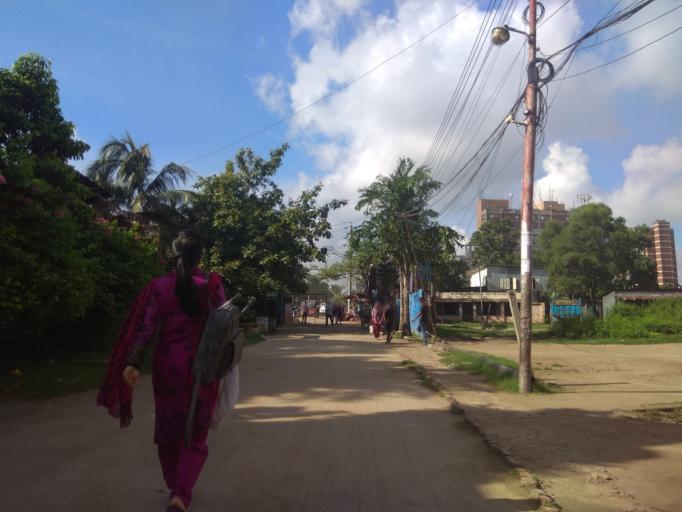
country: BD
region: Dhaka
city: Paltan
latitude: 23.8059
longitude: 90.3879
